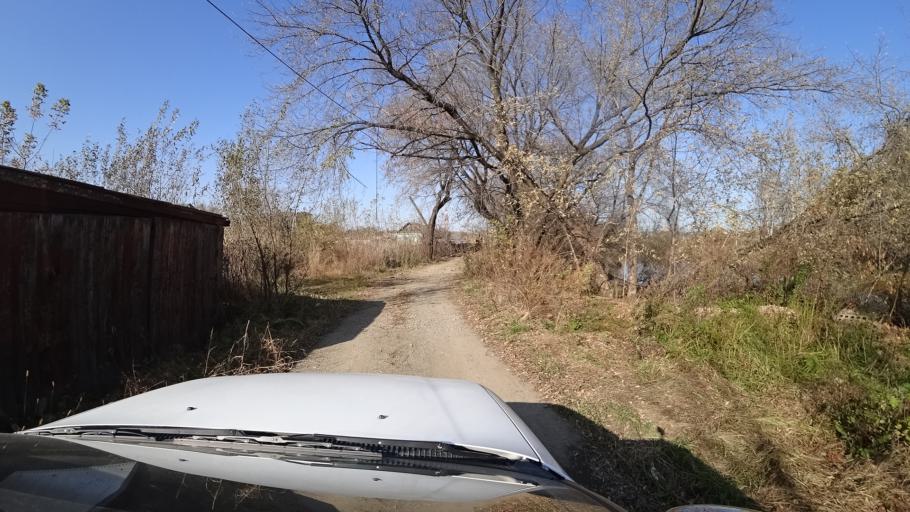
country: RU
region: Primorskiy
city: Dal'nerechensk
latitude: 45.9266
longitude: 133.7265
